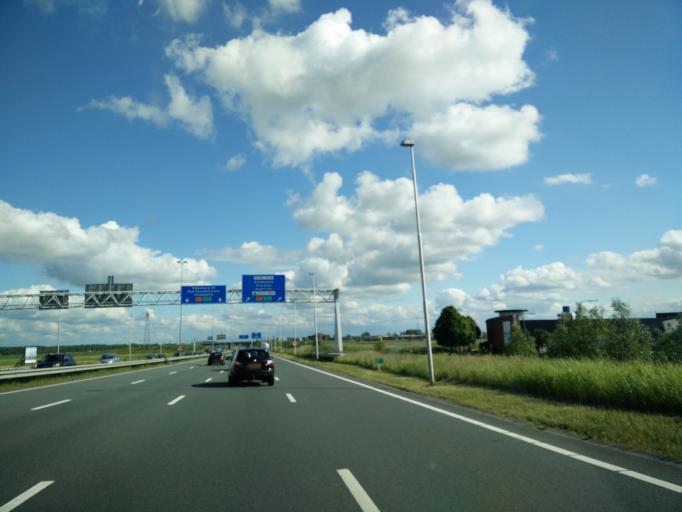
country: NL
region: Groningen
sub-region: Gemeente Groningen
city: Oosterpark
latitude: 53.2220
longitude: 6.6148
